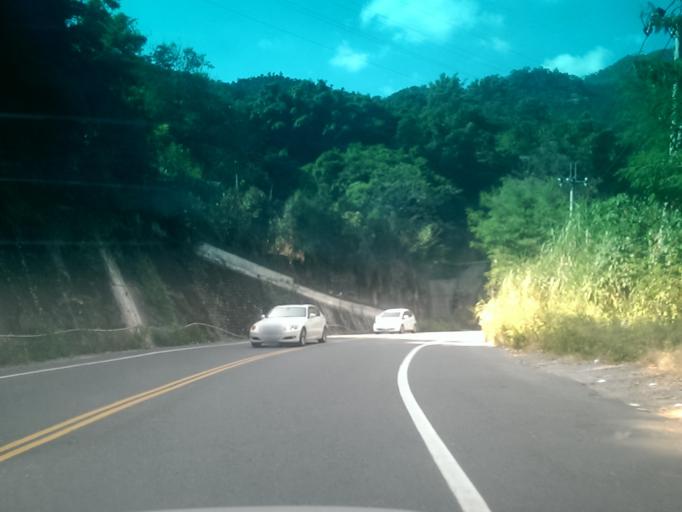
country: TW
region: Taiwan
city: Lugu
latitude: 23.8222
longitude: 120.8564
